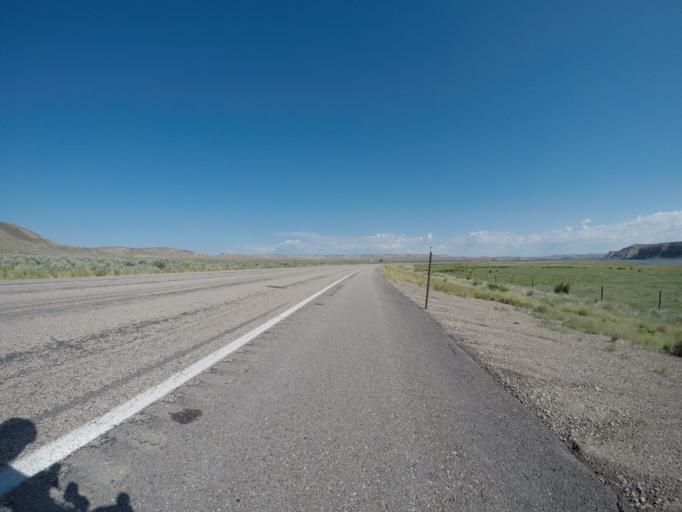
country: US
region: Wyoming
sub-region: Sublette County
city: Marbleton
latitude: 42.1252
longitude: -110.1872
